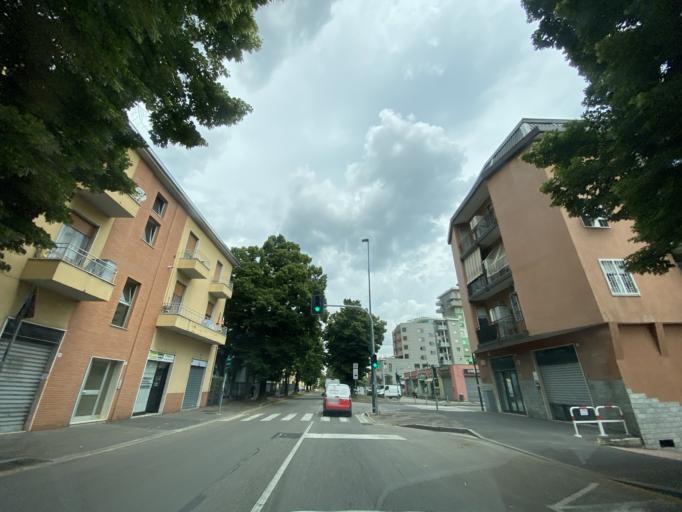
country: IT
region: Lombardy
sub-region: Citta metropolitana di Milano
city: Sesto San Giovanni
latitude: 45.5255
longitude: 9.2497
